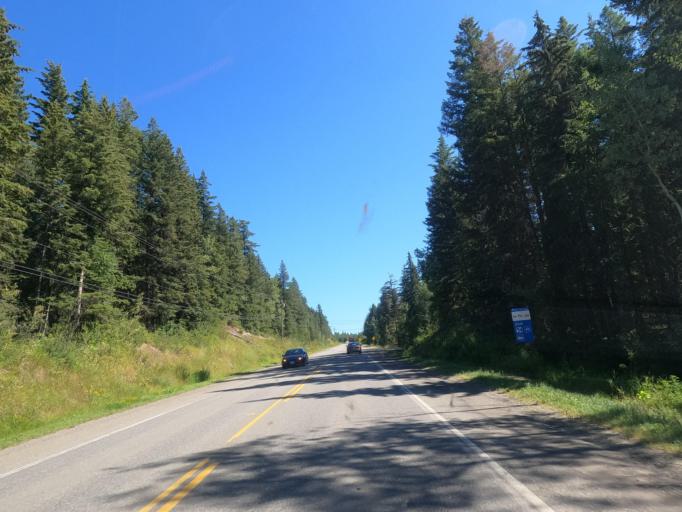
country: CA
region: British Columbia
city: Quesnel
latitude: 53.0486
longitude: -122.4616
